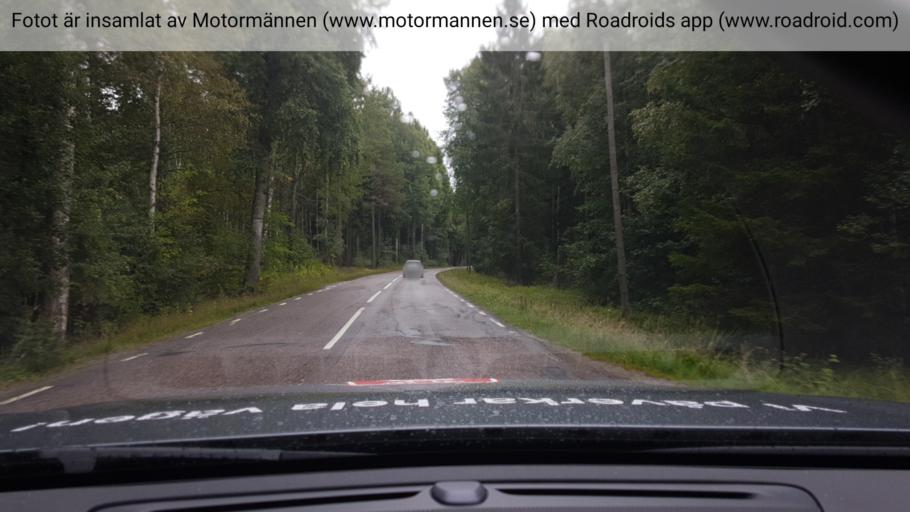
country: SE
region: Stockholm
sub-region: Botkyrka Kommun
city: Varsta
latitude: 59.1168
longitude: 17.8571
